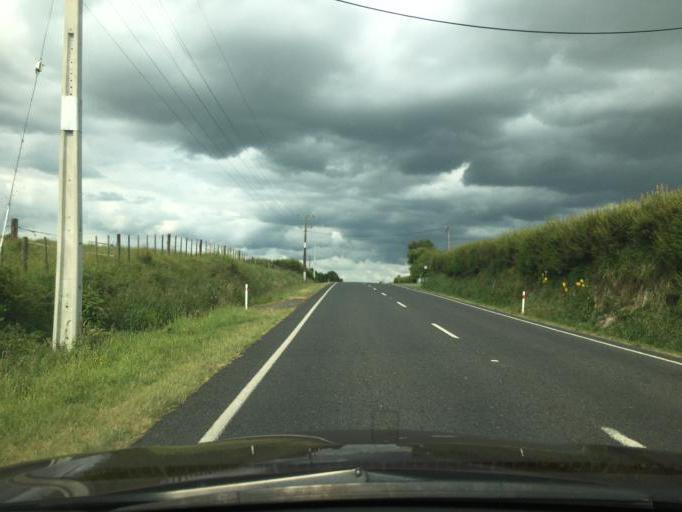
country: NZ
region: Waikato
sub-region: Waipa District
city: Cambridge
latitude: -38.0026
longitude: 175.3873
